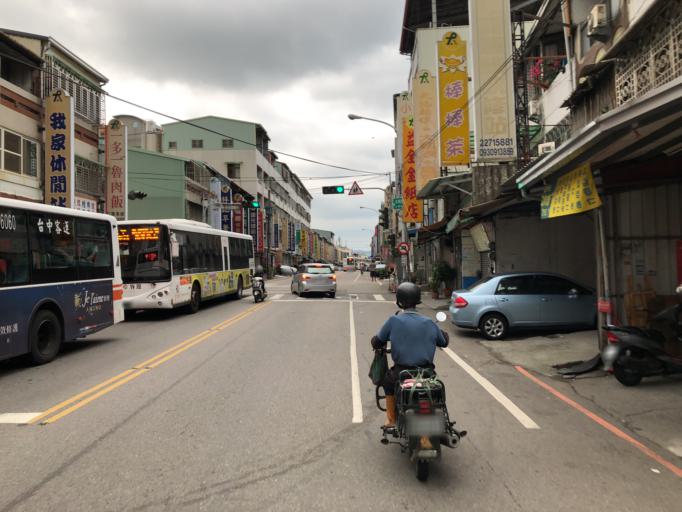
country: TW
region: Taiwan
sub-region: Taichung City
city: Taichung
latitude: 24.1040
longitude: 120.7290
